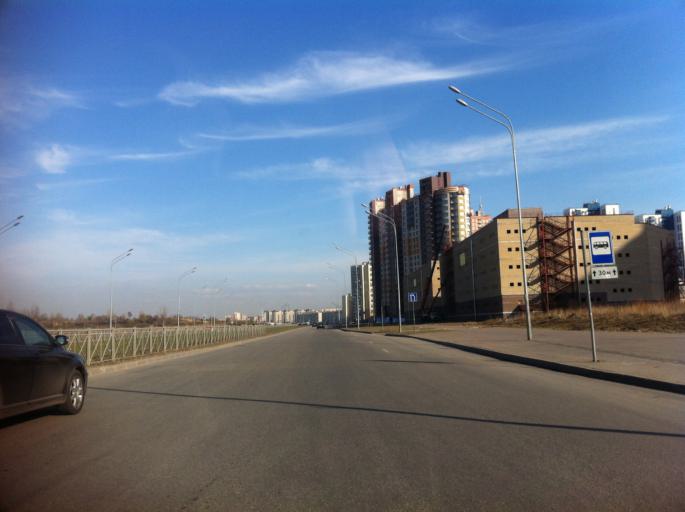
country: RU
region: St.-Petersburg
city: Uritsk
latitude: 59.8652
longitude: 30.1833
